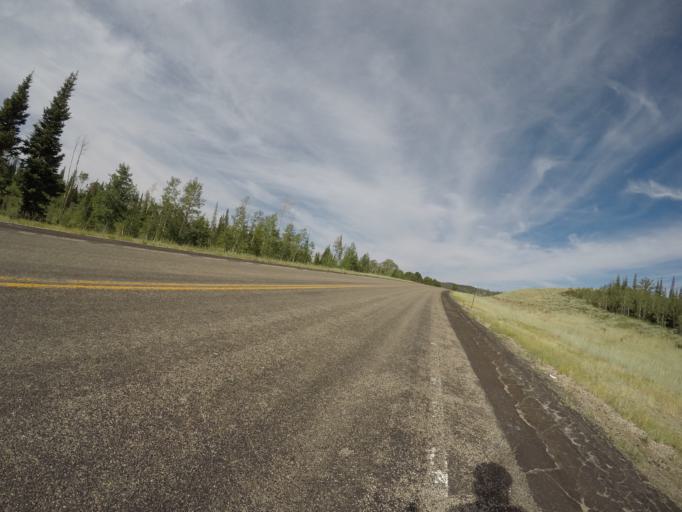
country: US
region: Wyoming
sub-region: Carbon County
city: Saratoga
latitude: 41.1775
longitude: -106.8838
